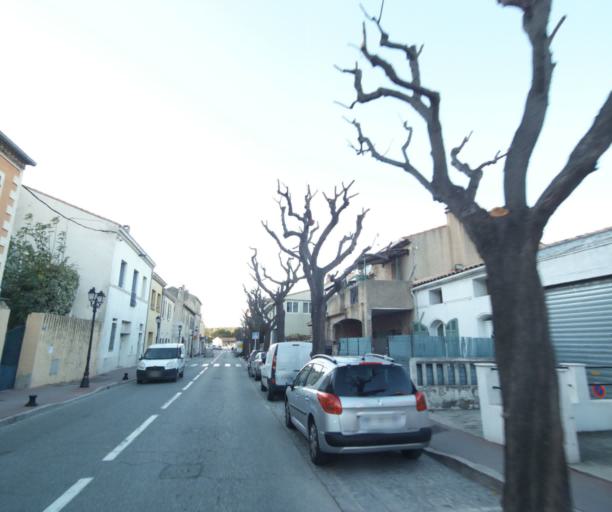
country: FR
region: Provence-Alpes-Cote d'Azur
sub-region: Departement des Bouches-du-Rhone
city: Roquefort-la-Bedoule
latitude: 43.2478
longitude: 5.5898
